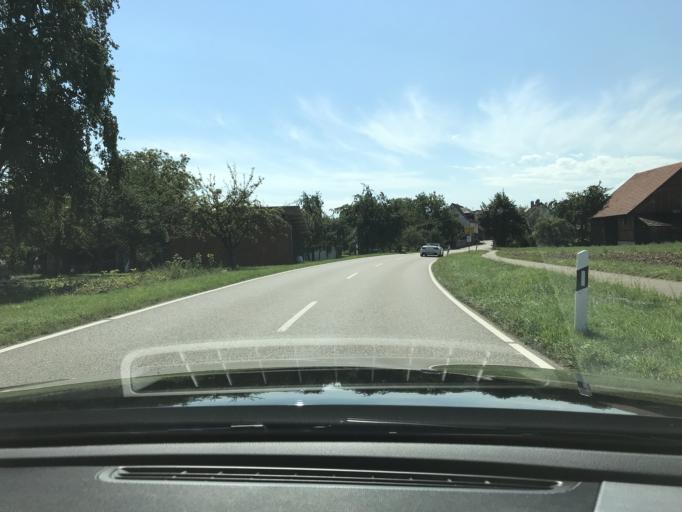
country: DE
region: Baden-Wuerttemberg
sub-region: Regierungsbezirk Stuttgart
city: Affalterbach
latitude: 48.9268
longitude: 9.3250
